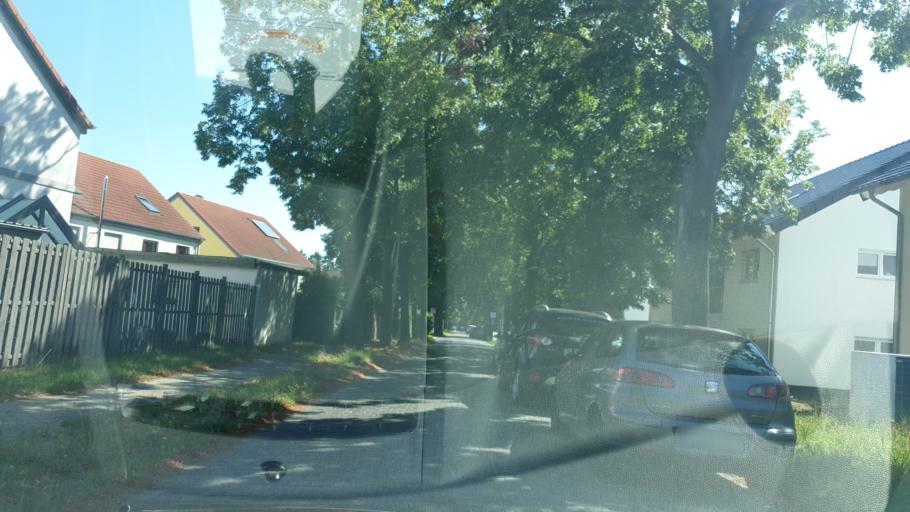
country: DE
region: North Rhine-Westphalia
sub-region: Regierungsbezirk Koln
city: Euskirchen
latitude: 50.6553
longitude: 6.7614
